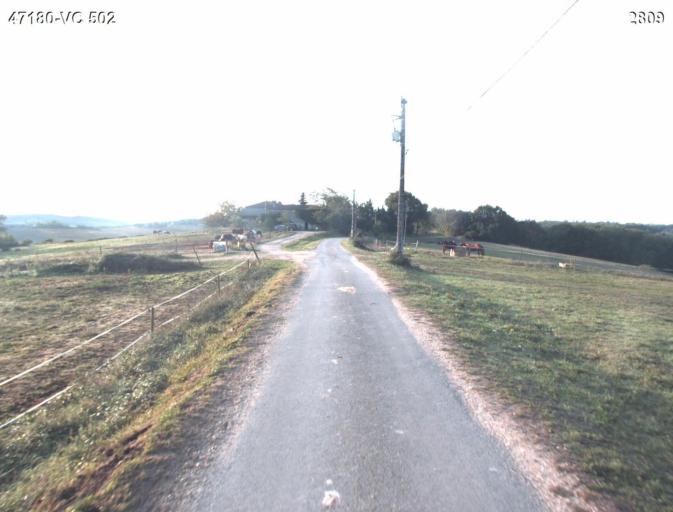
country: FR
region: Aquitaine
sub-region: Departement du Lot-et-Garonne
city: Sainte-Colombe-en-Bruilhois
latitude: 44.1818
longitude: 0.4828
